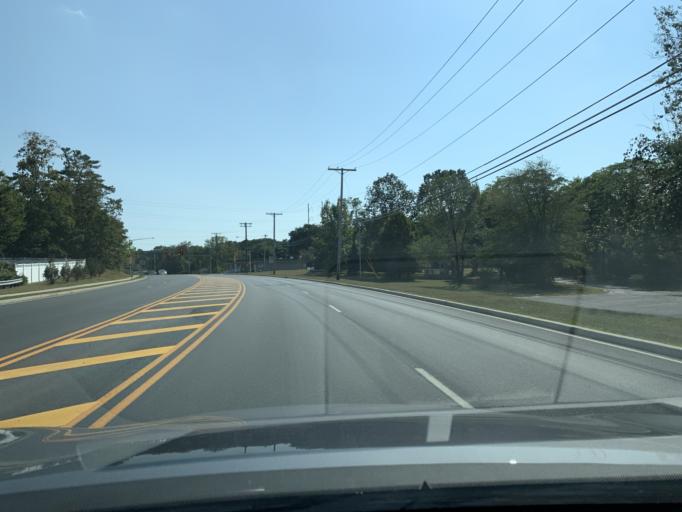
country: US
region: New Jersey
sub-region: Monmouth County
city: Tinton Falls
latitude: 40.2880
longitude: -74.0953
